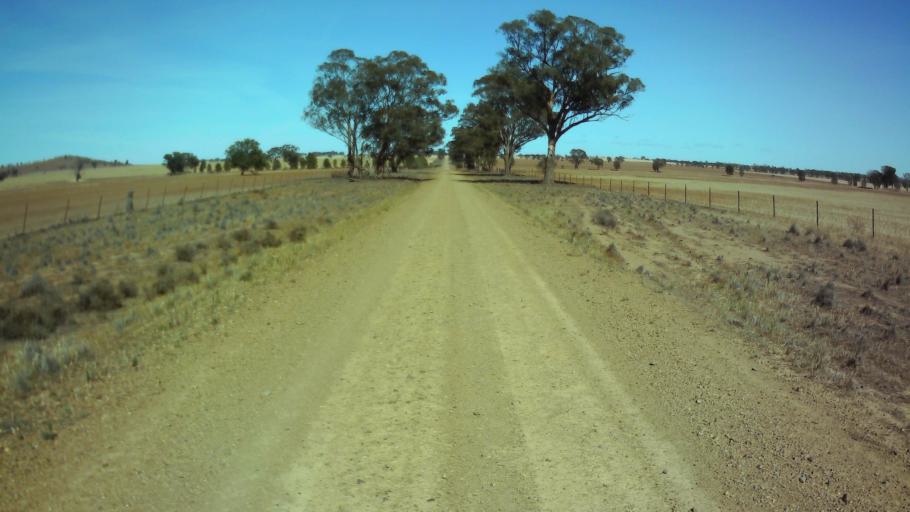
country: AU
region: New South Wales
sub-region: Weddin
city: Grenfell
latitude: -33.7513
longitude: 147.9025
